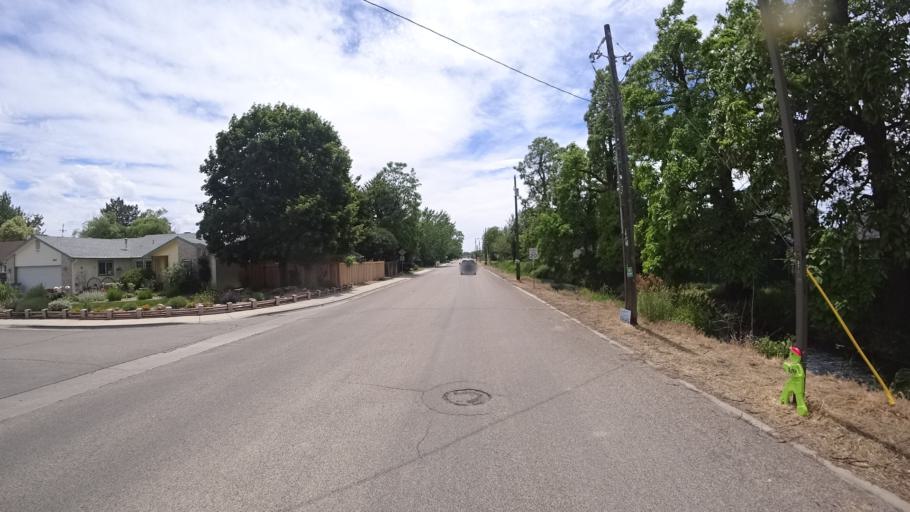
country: US
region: Idaho
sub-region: Ada County
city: Meridian
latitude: 43.6258
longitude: -116.3201
